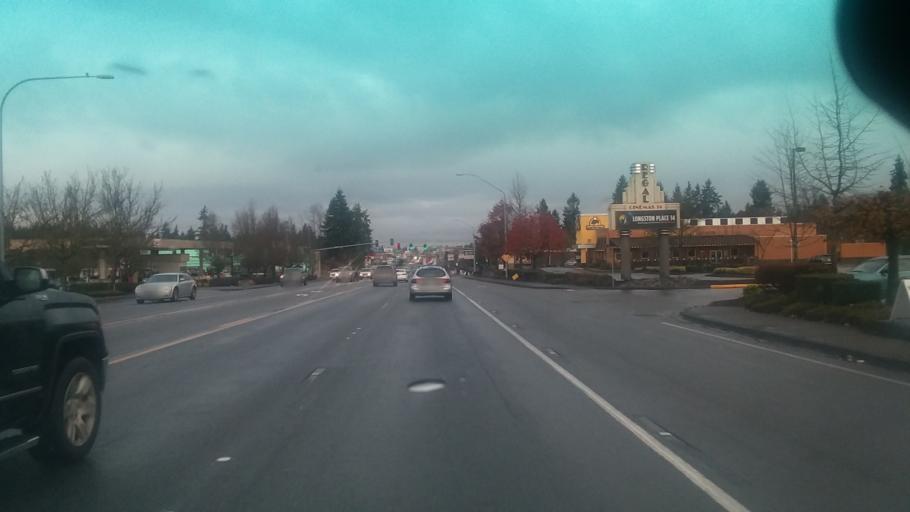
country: US
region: Washington
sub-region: Pierce County
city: South Hill
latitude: 47.1351
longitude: -122.2929
